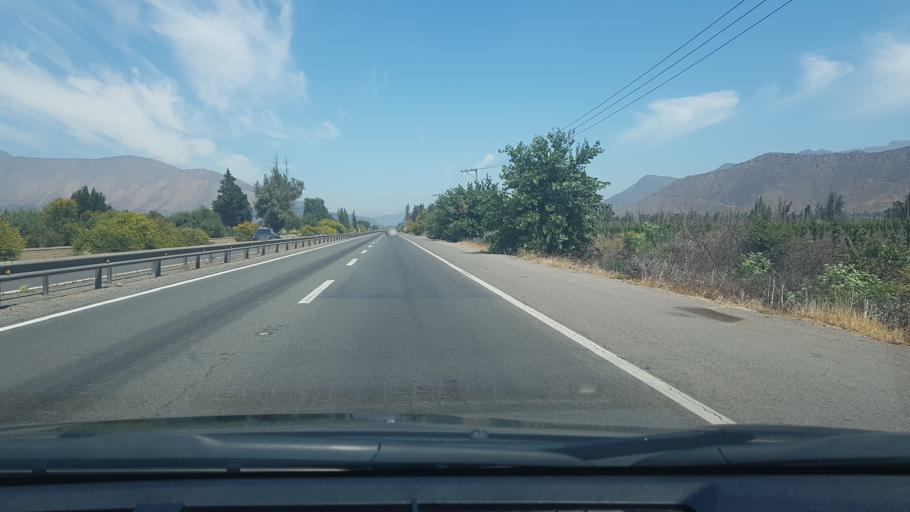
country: CL
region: Valparaiso
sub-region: Provincia de San Felipe
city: Llaillay
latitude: -32.8532
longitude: -70.9283
